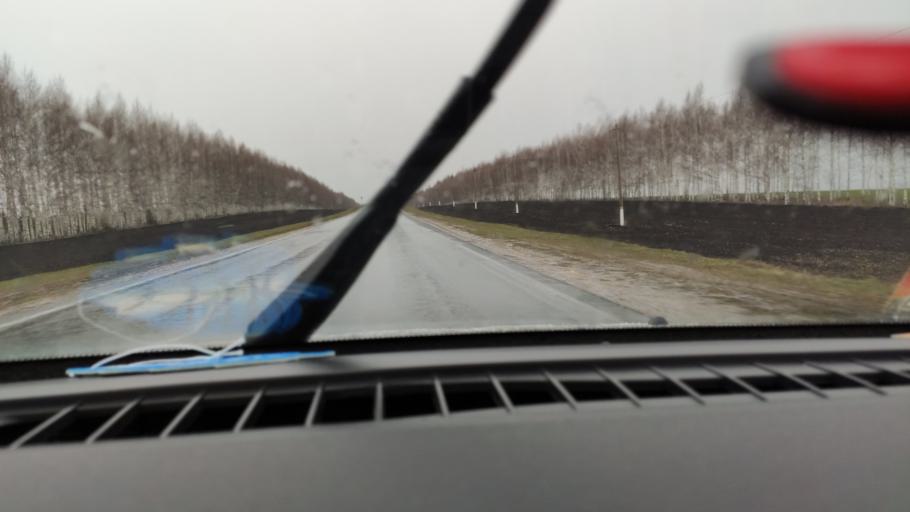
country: RU
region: Samara
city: Chelno-Vershiny
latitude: 54.6814
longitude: 51.0795
